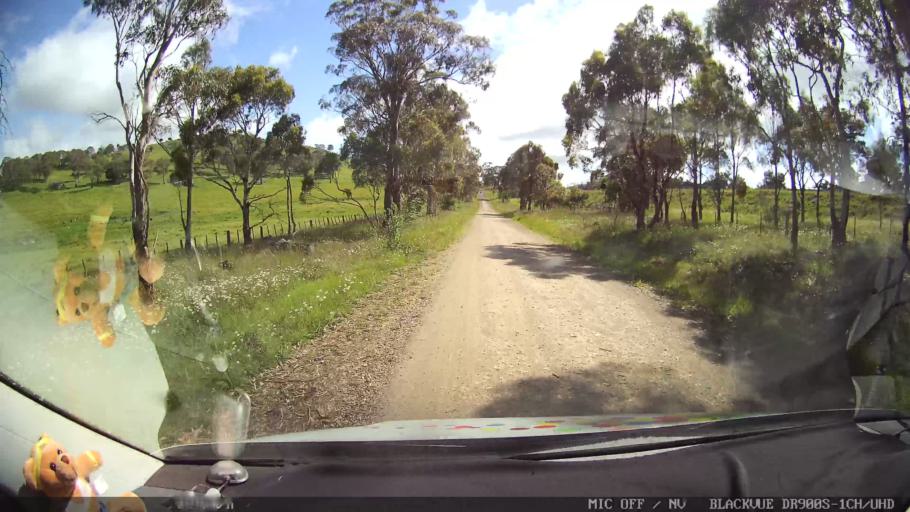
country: AU
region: New South Wales
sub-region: Guyra
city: Guyra
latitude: -30.0109
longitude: 151.6597
